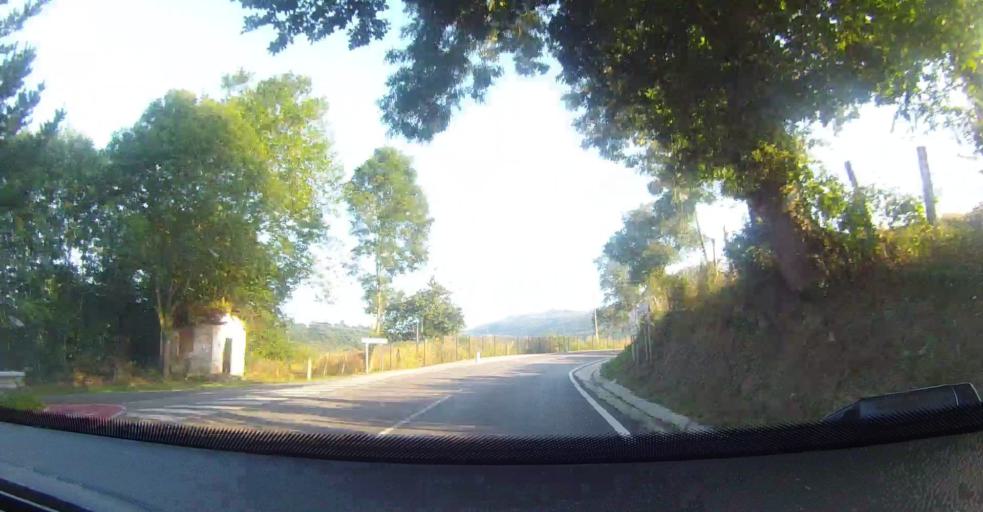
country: ES
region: Cantabria
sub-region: Provincia de Cantabria
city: Rasines
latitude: 43.3130
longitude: -3.4246
